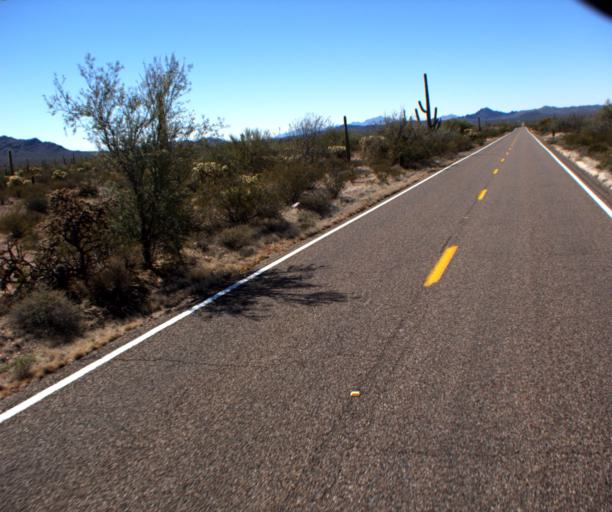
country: MX
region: Sonora
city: Sonoyta
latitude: 32.0703
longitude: -112.7833
